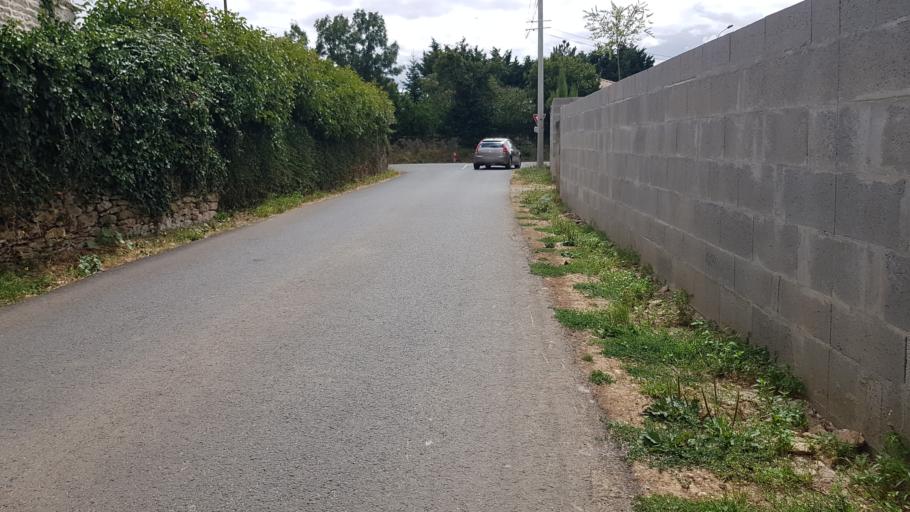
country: FR
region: Poitou-Charentes
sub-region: Departement des Deux-Sevres
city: Vouille
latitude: 46.3045
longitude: -0.3349
